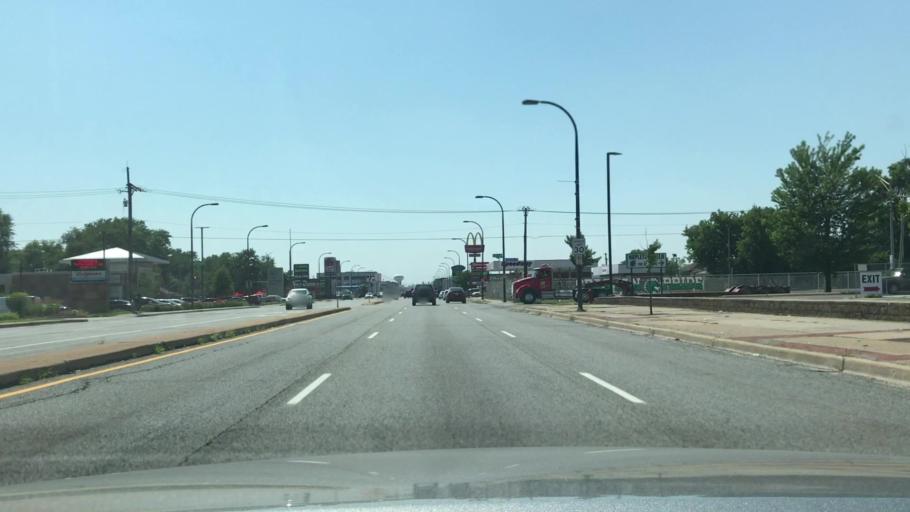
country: US
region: Illinois
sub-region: Cook County
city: Oak Lawn
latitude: 41.7197
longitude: -87.7694
